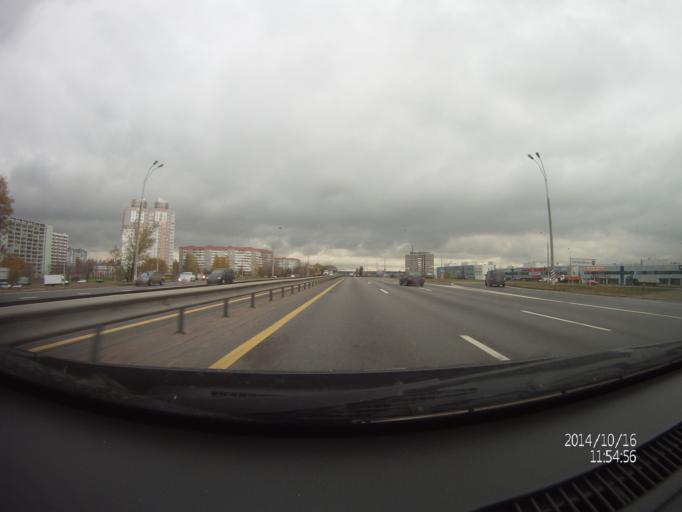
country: BY
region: Minsk
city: Vyaliki Trastsyanets
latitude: 53.8608
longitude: 27.6826
